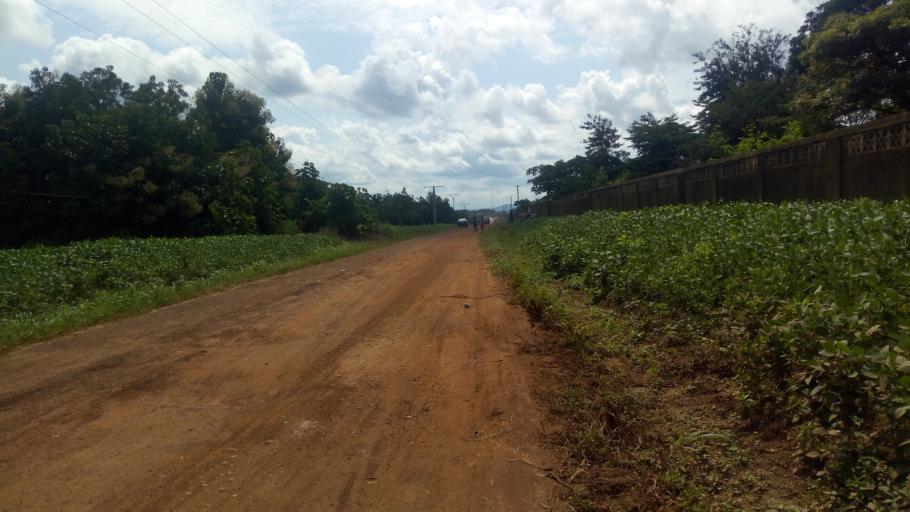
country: TG
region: Centrale
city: Sotouboua
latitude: 8.4329
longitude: 1.0018
